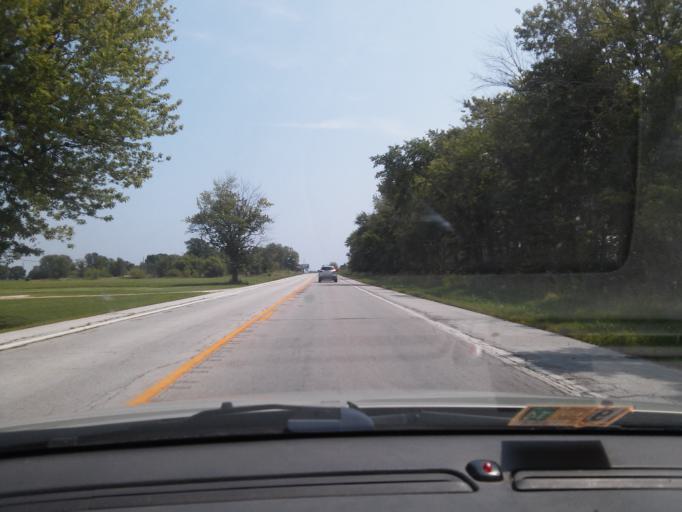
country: US
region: Missouri
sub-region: Audrain County
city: Vandalia
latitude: 39.3149
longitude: -91.4752
